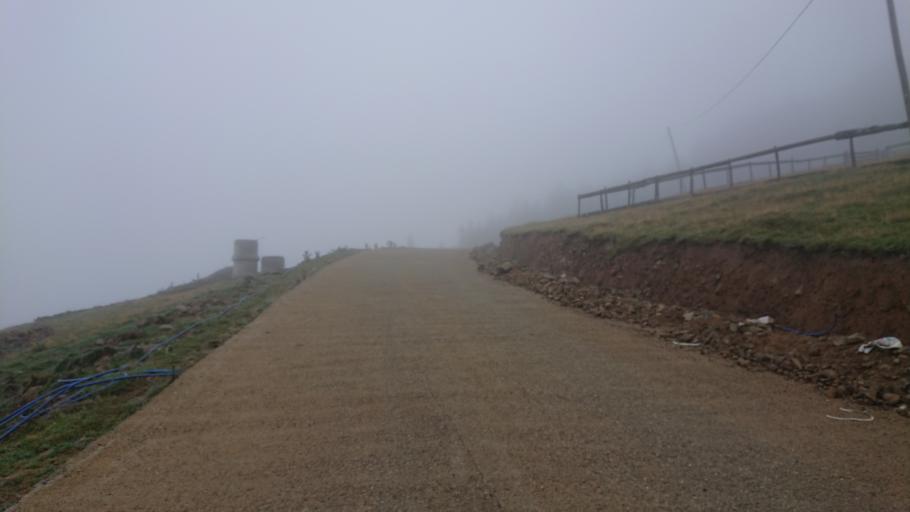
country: TR
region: Gumushane
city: Kurtun
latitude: 40.6719
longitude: 38.9971
